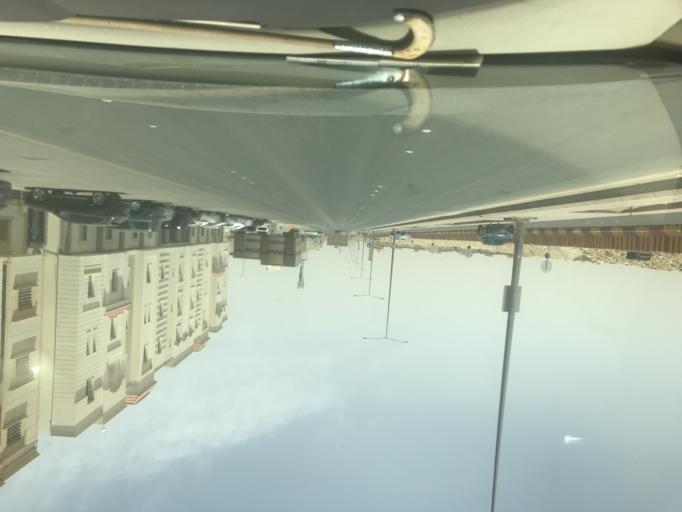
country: SA
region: Ar Riyad
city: Riyadh
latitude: 24.7948
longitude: 46.6682
